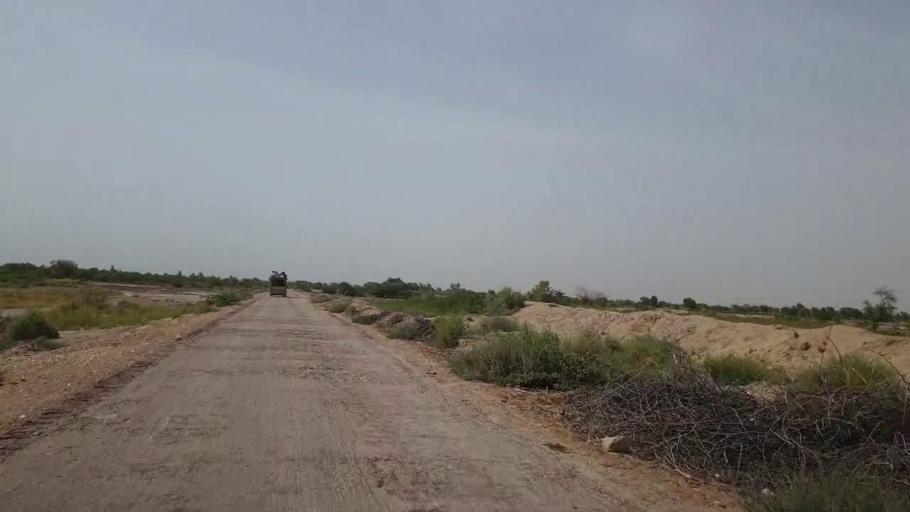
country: PK
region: Sindh
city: Bandhi
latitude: 26.5635
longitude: 68.3813
